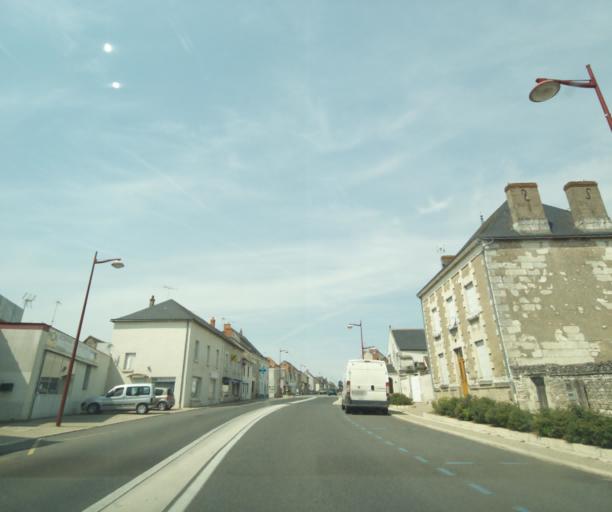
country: FR
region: Centre
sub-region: Departement d'Indre-et-Loire
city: La Celle-Saint-Avant
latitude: 47.0212
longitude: 0.6038
